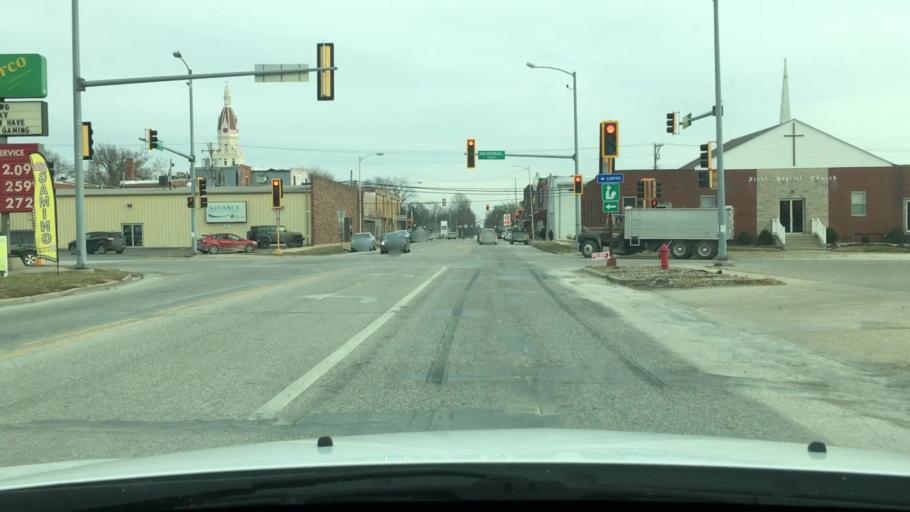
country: US
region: Illinois
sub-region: Pike County
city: Pittsfield
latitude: 39.6067
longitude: -90.8081
